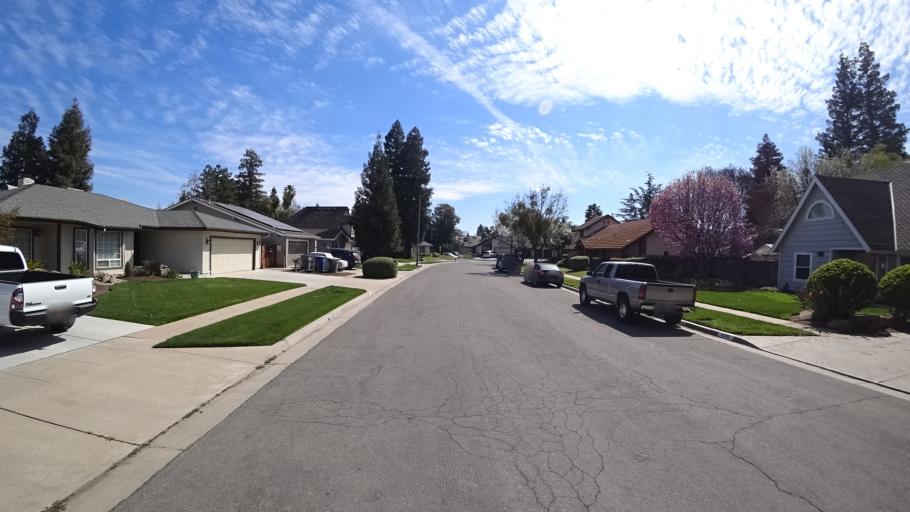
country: US
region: California
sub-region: Fresno County
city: Clovis
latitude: 36.8562
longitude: -119.7779
